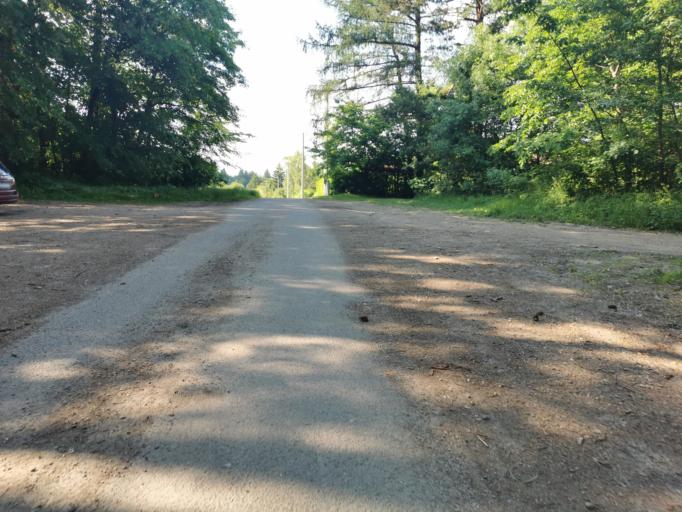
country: CZ
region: South Moravian
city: Knezdub
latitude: 48.8446
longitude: 17.3509
